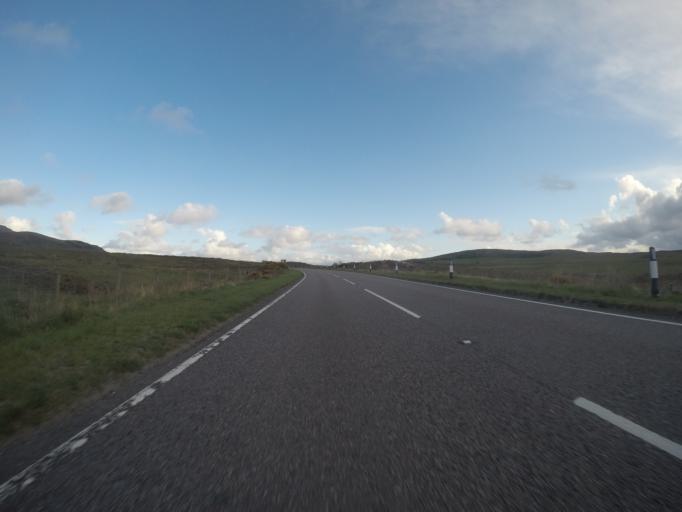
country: GB
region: Scotland
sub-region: Highland
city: Portree
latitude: 57.4761
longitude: -6.2998
